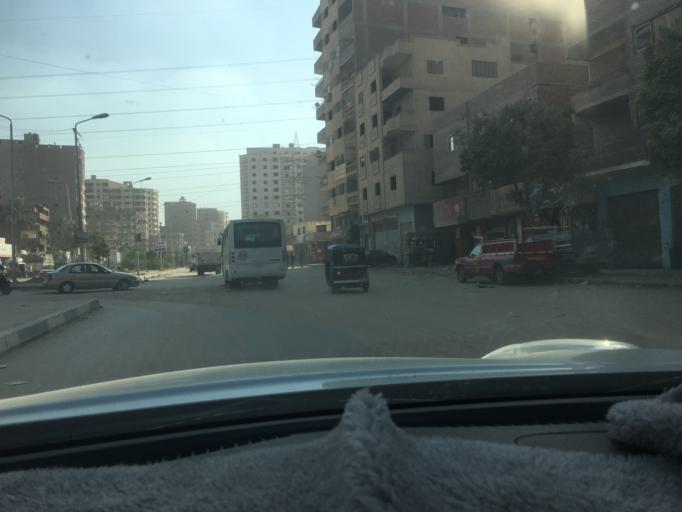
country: EG
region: Muhafazat al Qalyubiyah
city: Al Khankah
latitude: 30.1445
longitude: 31.3605
